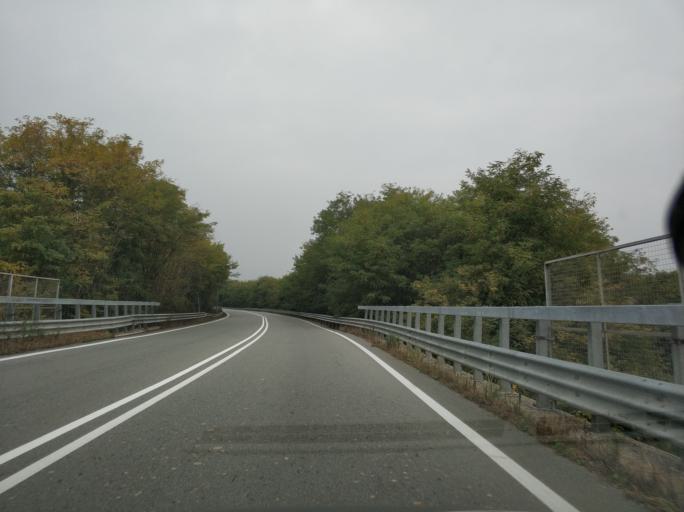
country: IT
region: Piedmont
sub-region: Provincia di Torino
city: Lombardore
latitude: 45.2319
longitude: 7.7487
